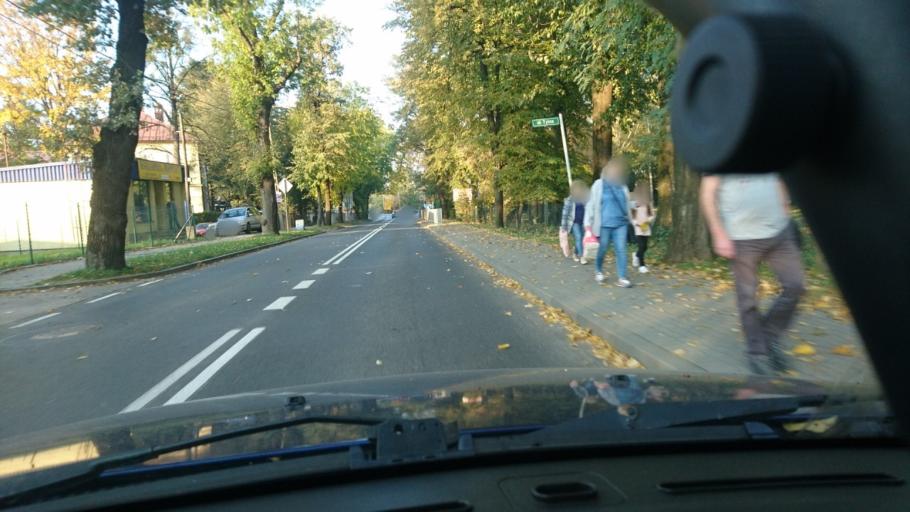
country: PL
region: Silesian Voivodeship
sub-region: Powiat bielski
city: Jaworze
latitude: 49.8068
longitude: 18.9820
